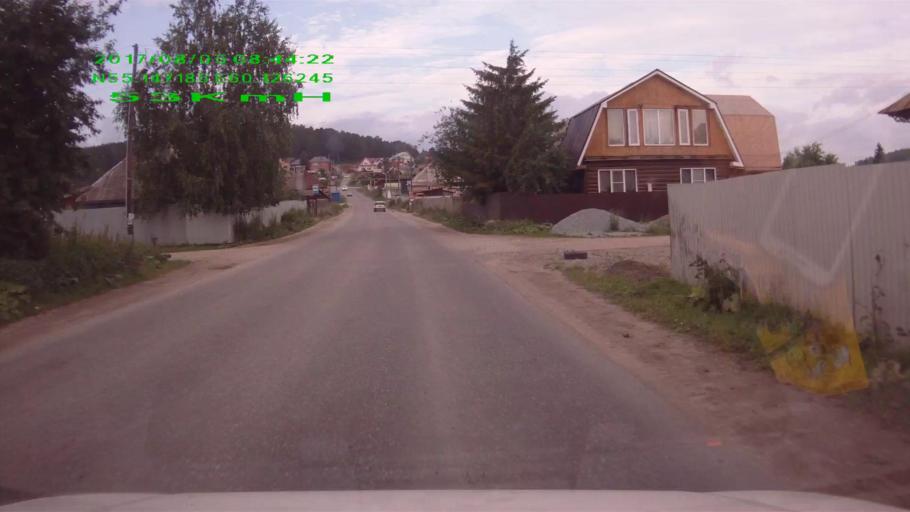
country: RU
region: Chelyabinsk
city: Turgoyak
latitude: 55.1472
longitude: 60.1258
